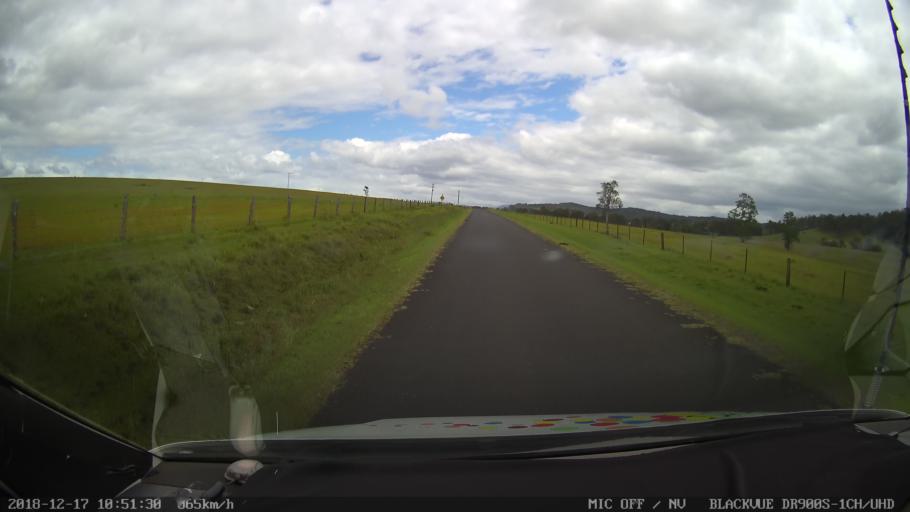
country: AU
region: New South Wales
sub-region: Tenterfield Municipality
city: Carrolls Creek
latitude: -28.8511
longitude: 152.5669
